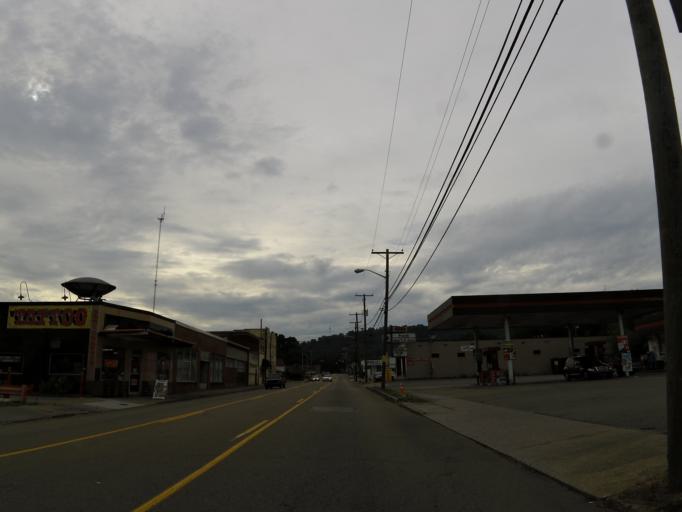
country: US
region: Tennessee
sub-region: Knox County
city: Knoxville
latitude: 35.9902
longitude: -83.9401
